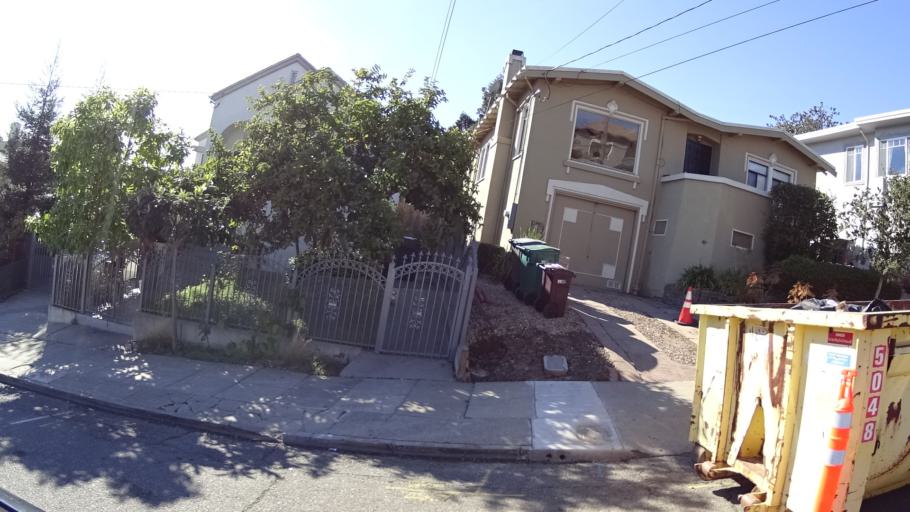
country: US
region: California
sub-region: Alameda County
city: Piedmont
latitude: 37.8139
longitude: -122.2403
